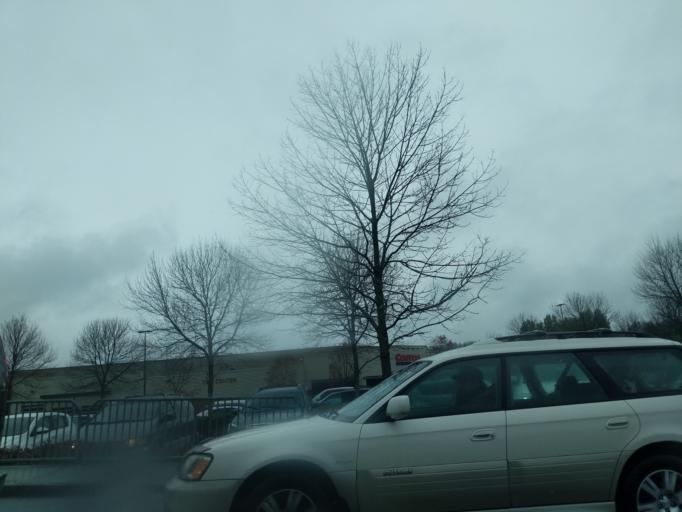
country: US
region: Washington
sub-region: King County
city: Woodinville
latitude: 47.7800
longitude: -122.1469
